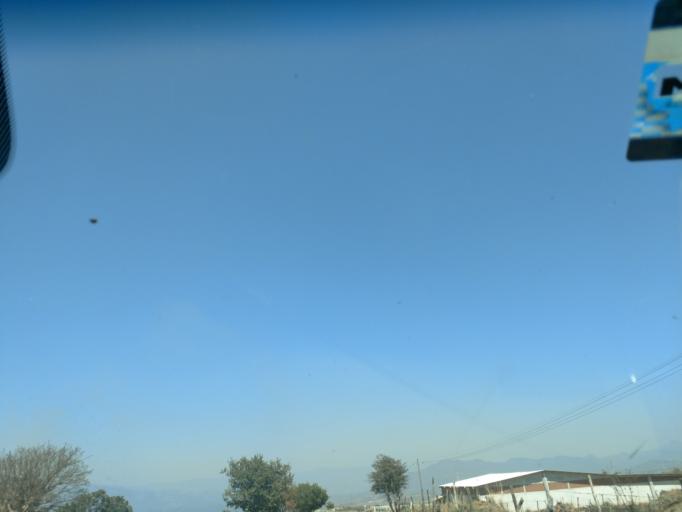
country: MX
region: Nayarit
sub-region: Tepic
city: La Corregidora
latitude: 21.4937
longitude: -104.6932
